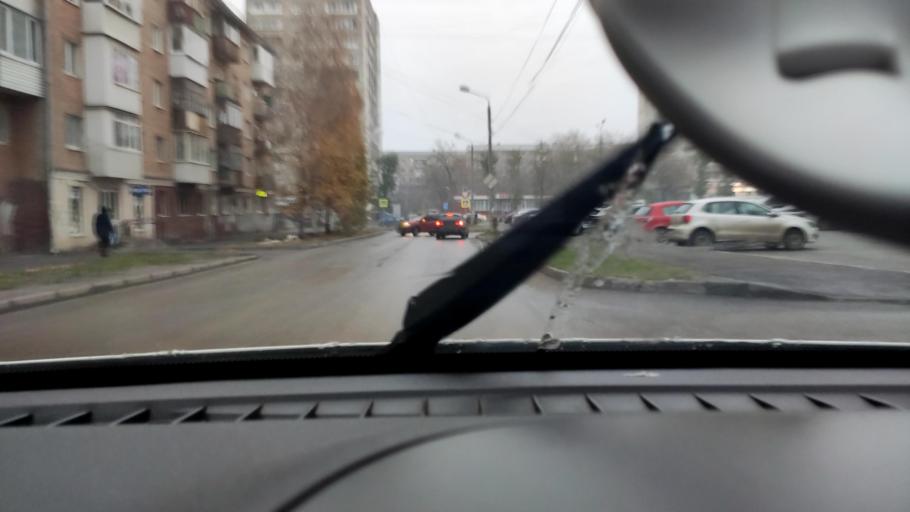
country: RU
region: Perm
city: Perm
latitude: 57.9764
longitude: 56.1831
